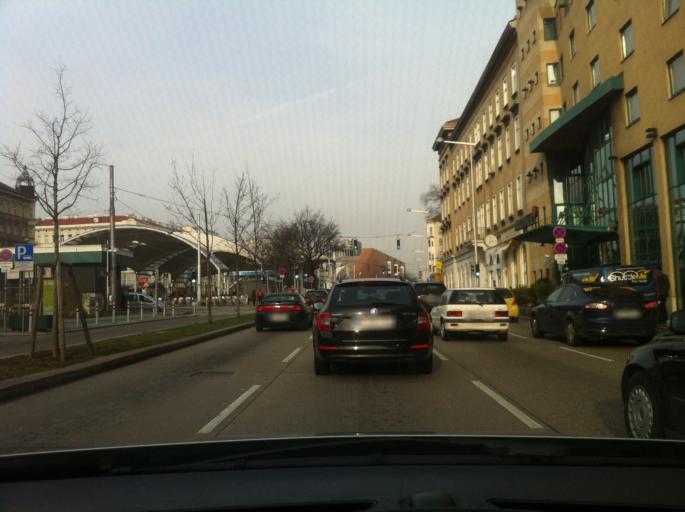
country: AT
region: Vienna
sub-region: Wien Stadt
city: Vienna
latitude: 48.2004
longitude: 16.3382
